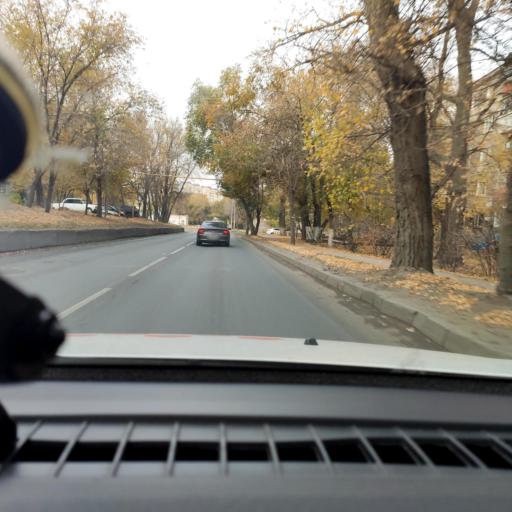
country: RU
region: Samara
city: Rozhdestveno
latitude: 53.1435
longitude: 50.0486
